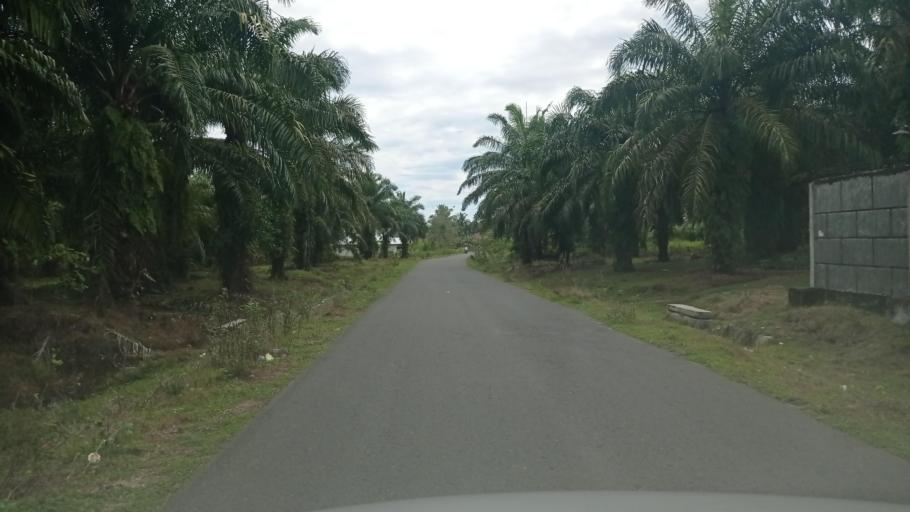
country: ID
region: Bengkulu
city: Ipuh
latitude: -2.5661
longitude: 101.1086
